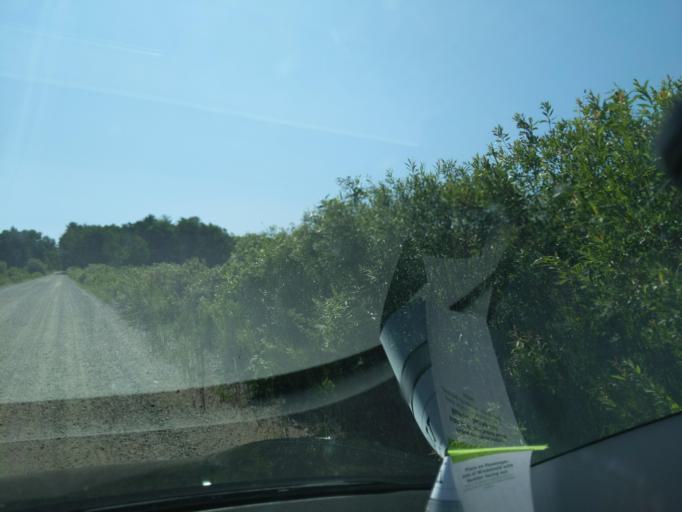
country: US
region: Michigan
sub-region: Cheboygan County
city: Cheboygan
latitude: 45.6792
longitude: -84.6603
